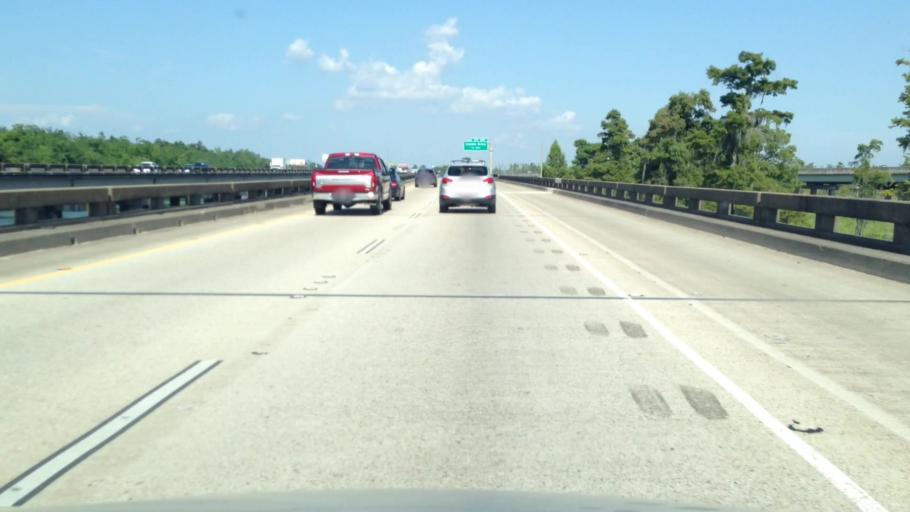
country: US
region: Louisiana
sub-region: Jefferson Parish
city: Kenner
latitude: 30.0058
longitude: -90.2887
